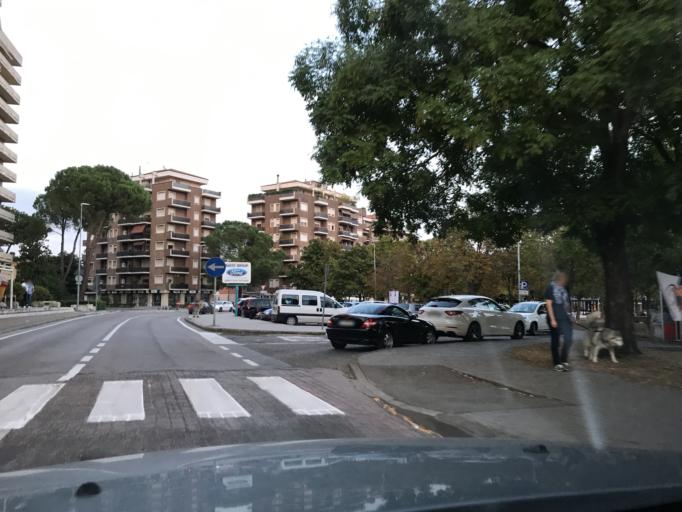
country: IT
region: Umbria
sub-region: Provincia di Perugia
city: Via Lippia
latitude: 43.0897
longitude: 12.4415
